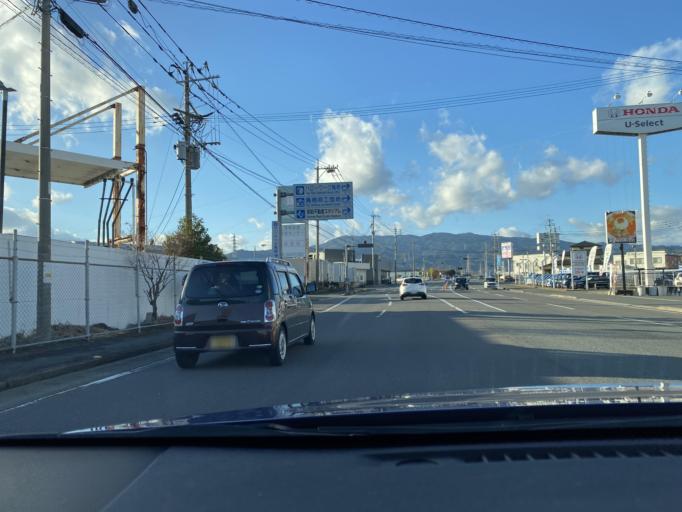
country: JP
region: Saga Prefecture
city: Tosu
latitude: 33.3591
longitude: 130.5077
